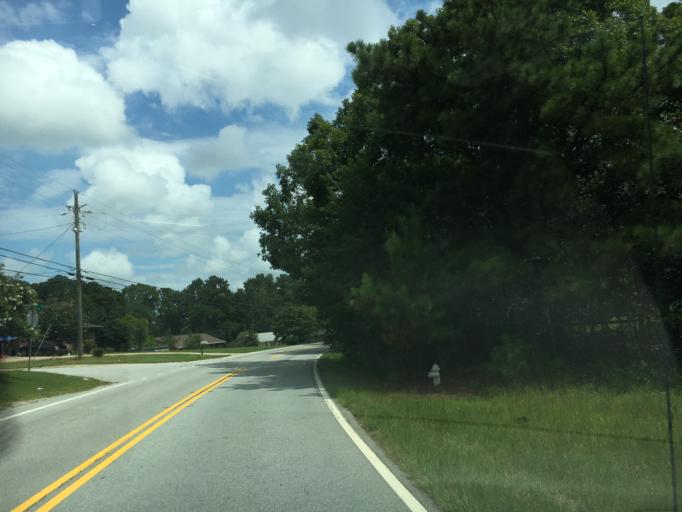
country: US
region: Georgia
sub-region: Rockdale County
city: Lakeview Estates
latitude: 33.6929
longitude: -84.0364
